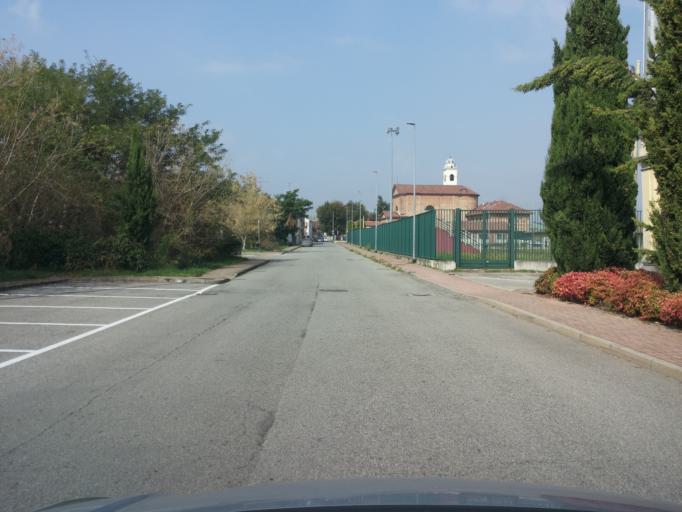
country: IT
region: Piedmont
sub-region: Provincia di Vercelli
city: Vercelli
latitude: 45.3036
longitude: 8.4488
